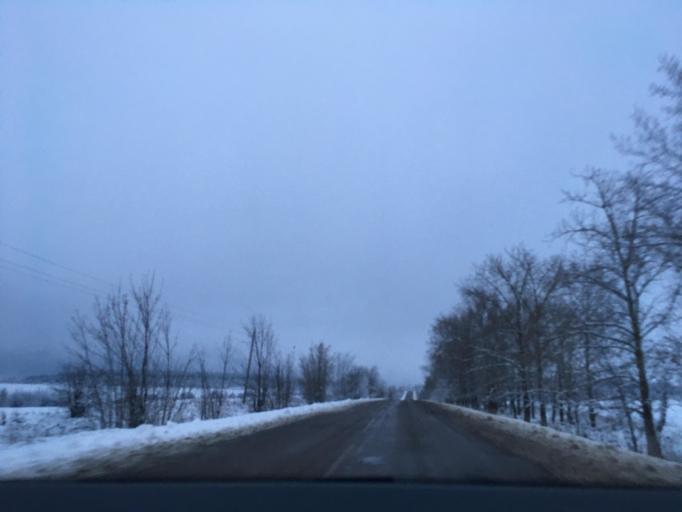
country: RU
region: Voronezj
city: Verkhniy Mamon
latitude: 50.0605
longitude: 40.2647
